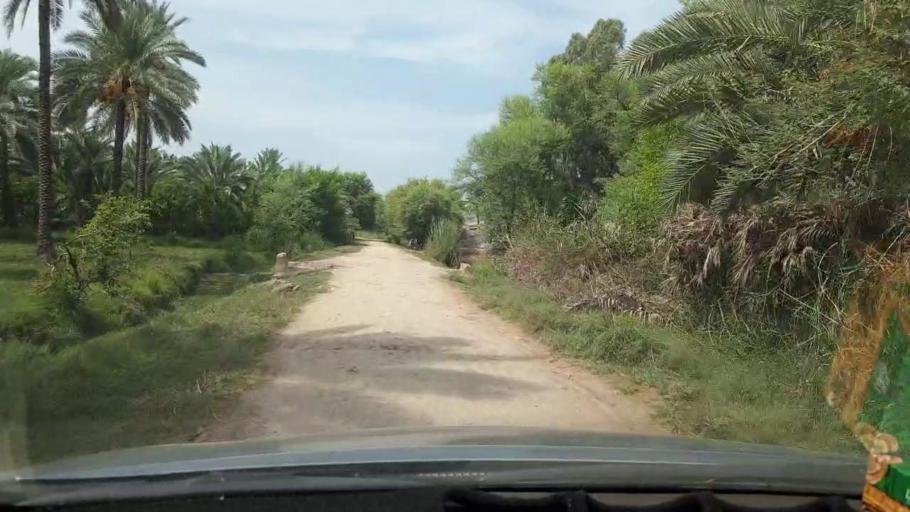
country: PK
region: Sindh
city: Khairpur
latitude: 27.4876
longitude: 68.7522
